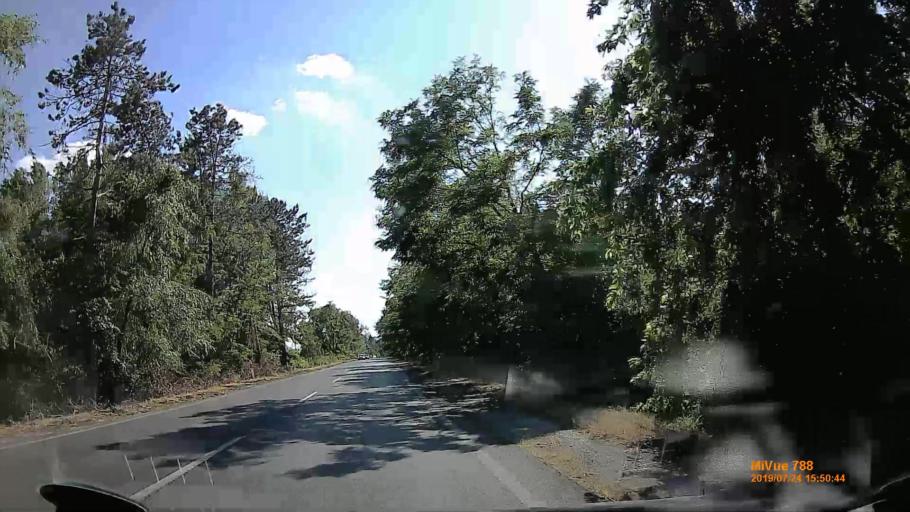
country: HU
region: Szabolcs-Szatmar-Bereg
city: Nyirmada
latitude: 48.0478
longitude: 22.1935
